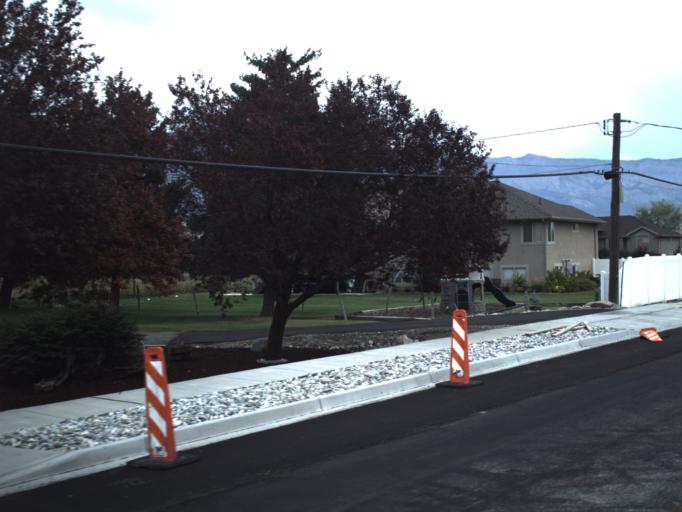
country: US
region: Utah
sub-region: Weber County
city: Plain City
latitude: 41.3051
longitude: -112.0620
